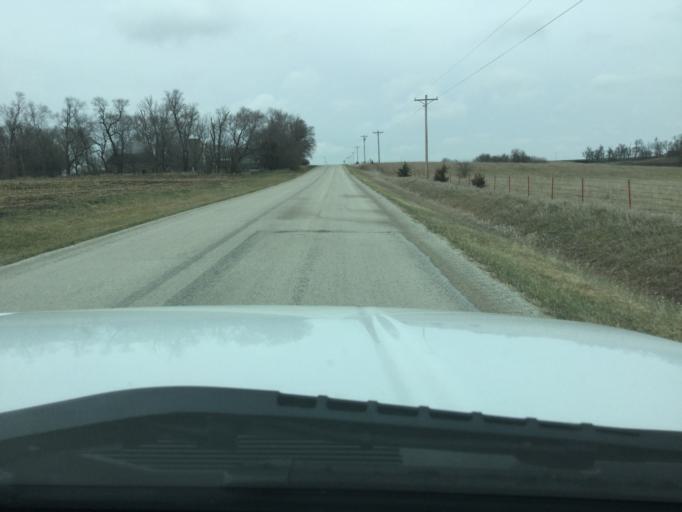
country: US
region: Kansas
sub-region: Nemaha County
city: Sabetha
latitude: 39.8763
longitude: -95.7141
